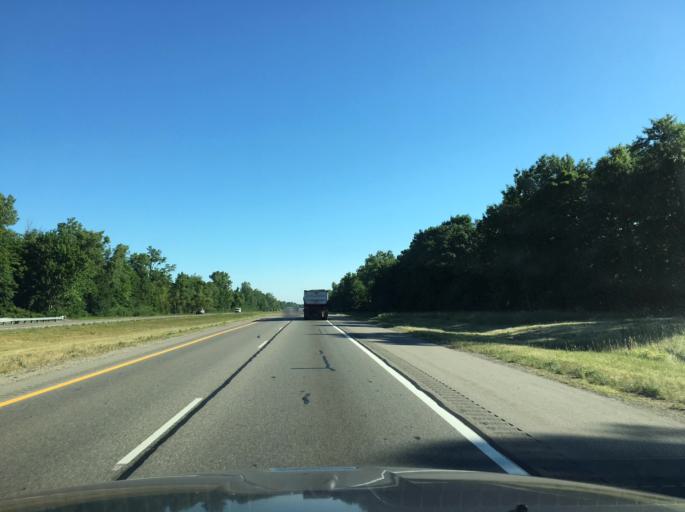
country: US
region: Michigan
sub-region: Macomb County
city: Shelby
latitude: 42.6556
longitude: -83.0141
